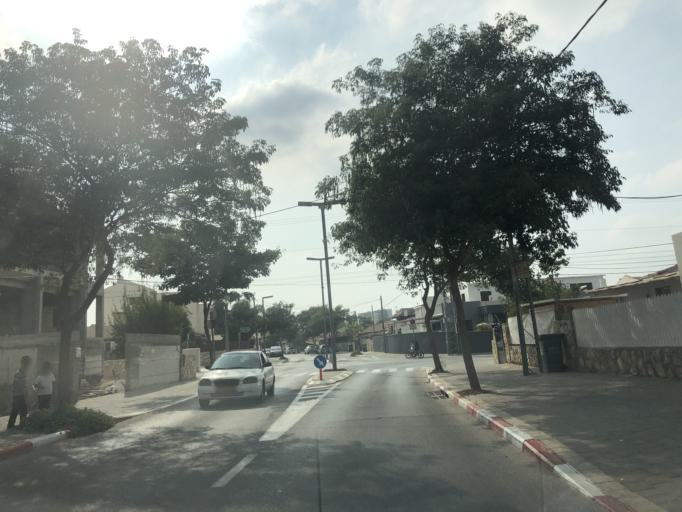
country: IL
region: Central District
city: Rosh Ha'Ayin
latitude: 32.0984
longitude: 34.9503
